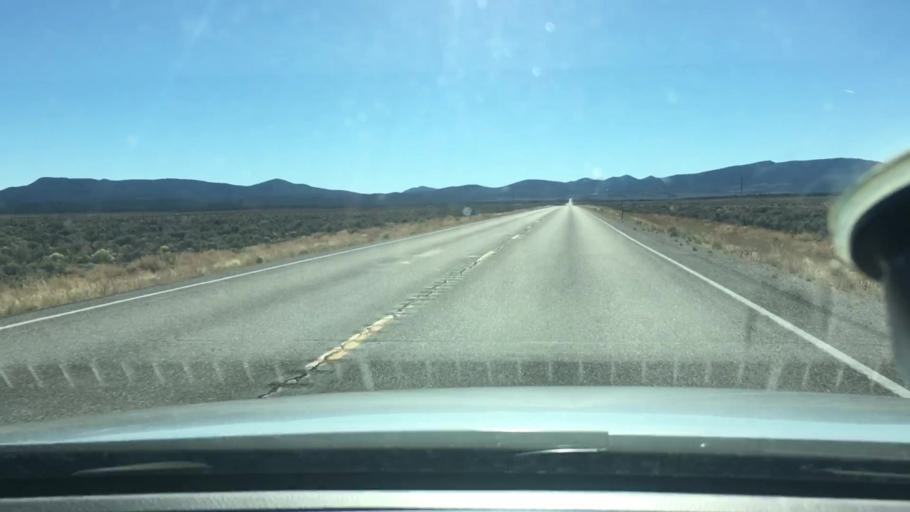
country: US
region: Nevada
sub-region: White Pine County
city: Ely
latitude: 38.8827
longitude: -115.2072
